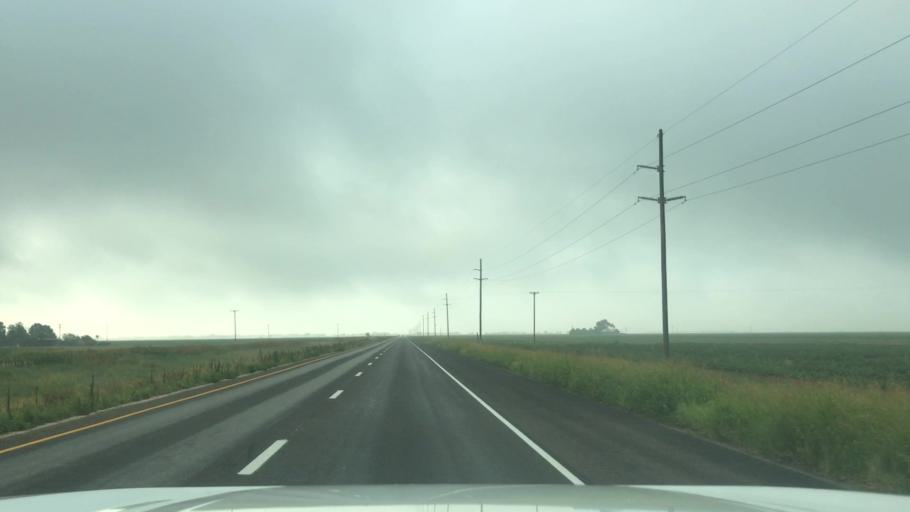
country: US
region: Texas
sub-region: Lubbock County
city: Slaton
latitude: 33.3756
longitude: -101.5787
